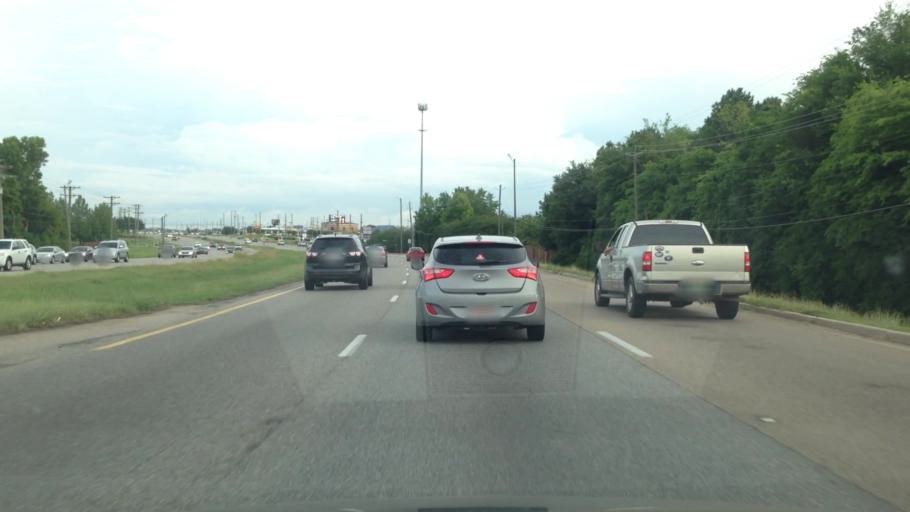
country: US
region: Alabama
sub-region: Montgomery County
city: Pike Road
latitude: 32.3451
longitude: -86.1791
